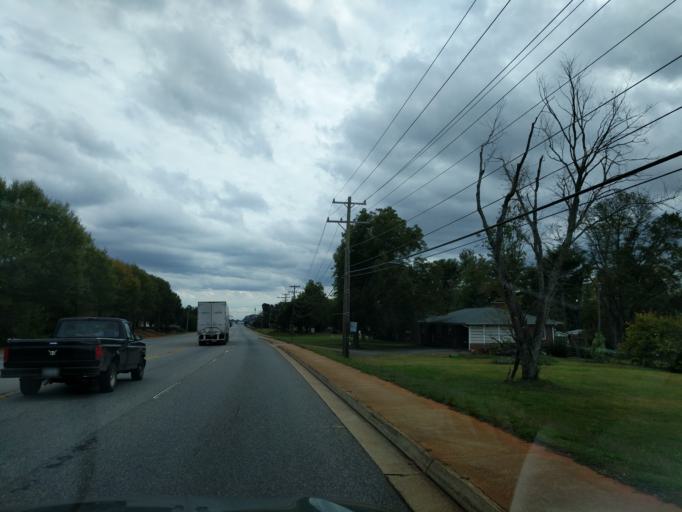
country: US
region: South Carolina
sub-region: Spartanburg County
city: Lyman
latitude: 34.9229
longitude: -82.1179
